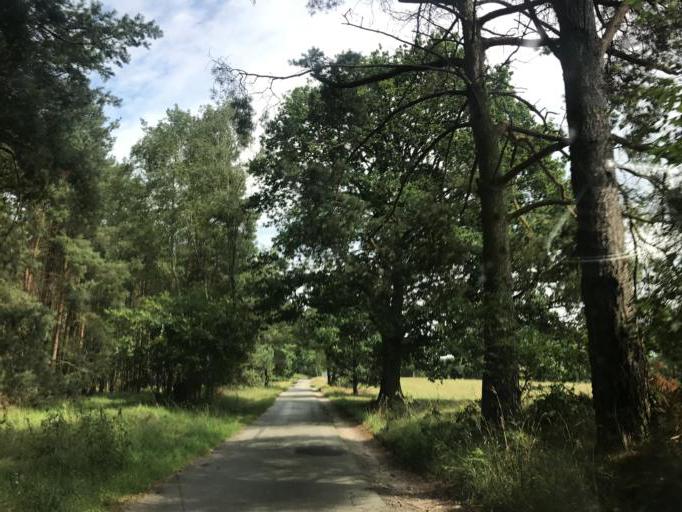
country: DE
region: Mecklenburg-Vorpommern
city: Wesenberg
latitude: 53.3597
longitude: 12.8676
